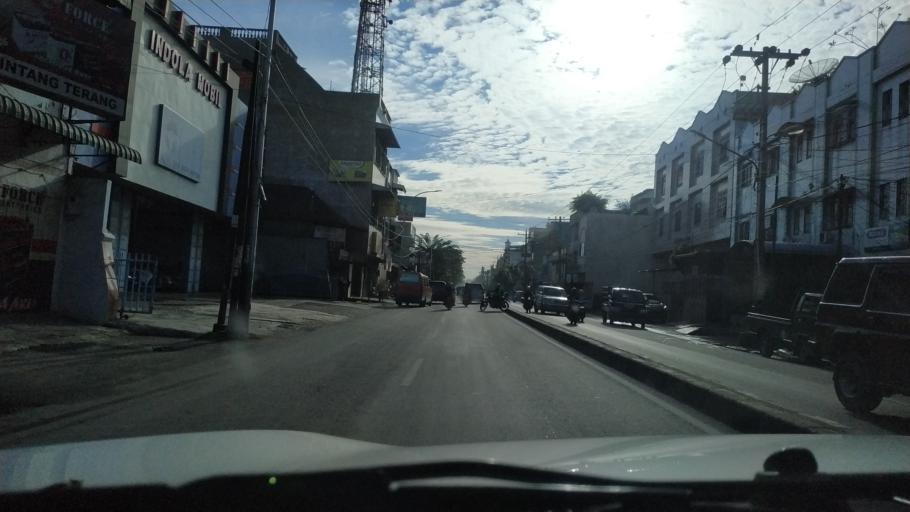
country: ID
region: North Sumatra
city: Medan
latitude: 3.5984
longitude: 98.6964
